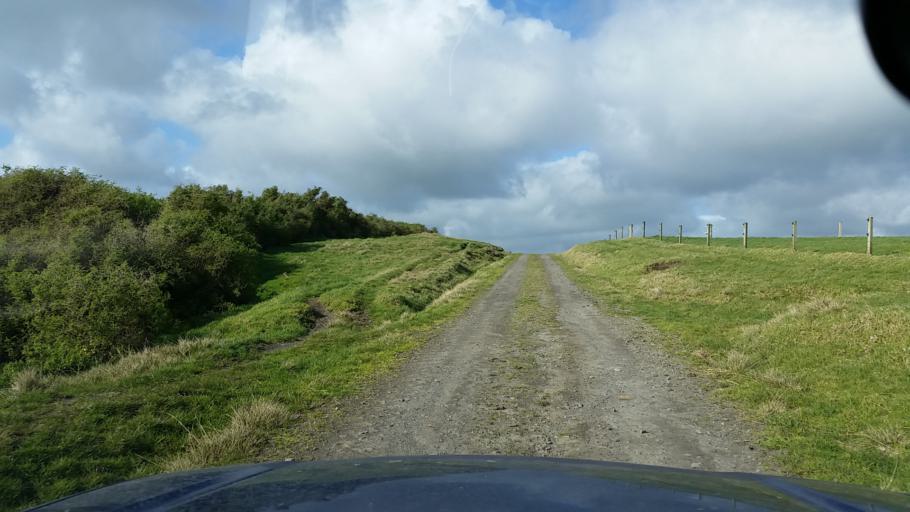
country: NZ
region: Taranaki
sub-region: South Taranaki District
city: Hawera
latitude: -39.6585
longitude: 174.3564
